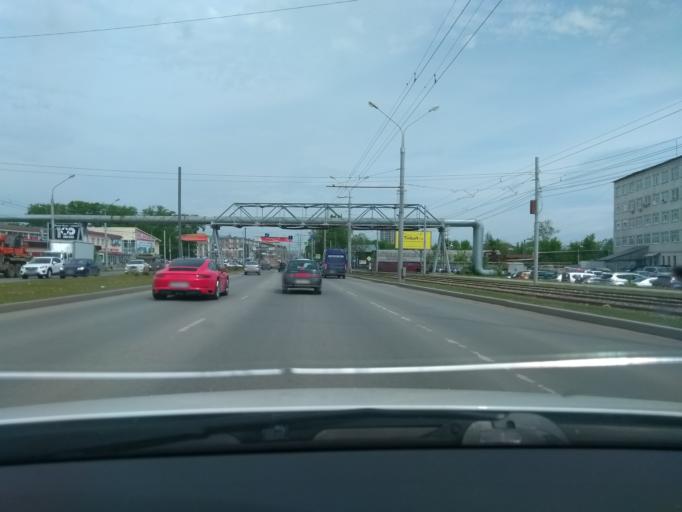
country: RU
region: Perm
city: Perm
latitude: 57.9825
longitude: 56.2590
